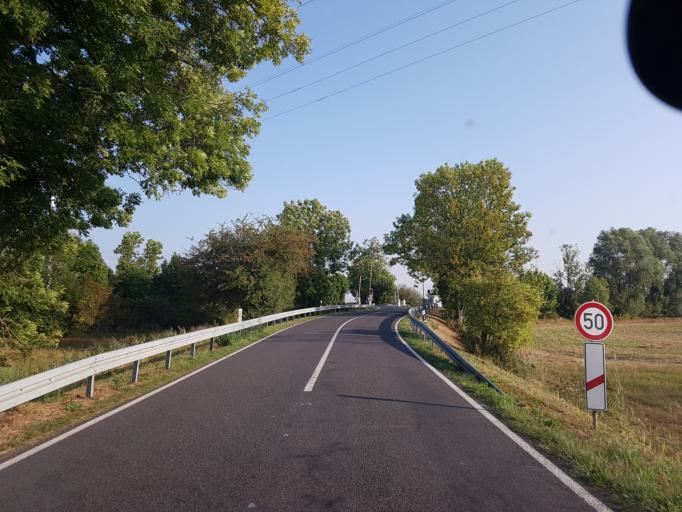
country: DE
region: Brandenburg
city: Finsterwalde
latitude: 51.6463
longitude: 13.7347
